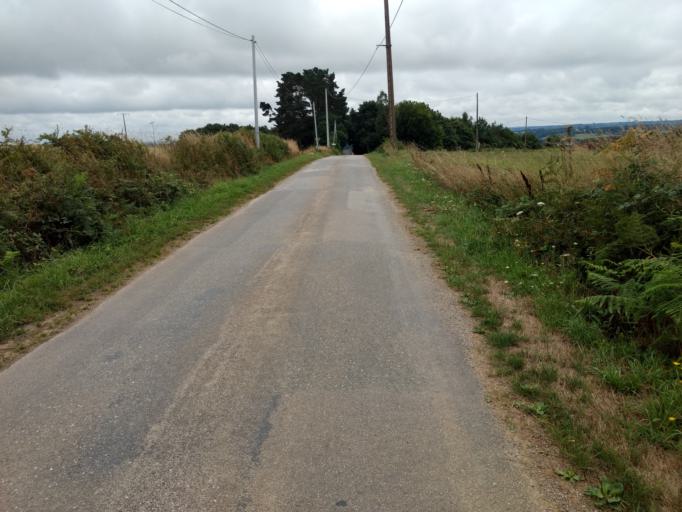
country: FR
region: Brittany
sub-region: Departement du Finistere
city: Loperhet
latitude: 48.3642
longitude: -4.2895
